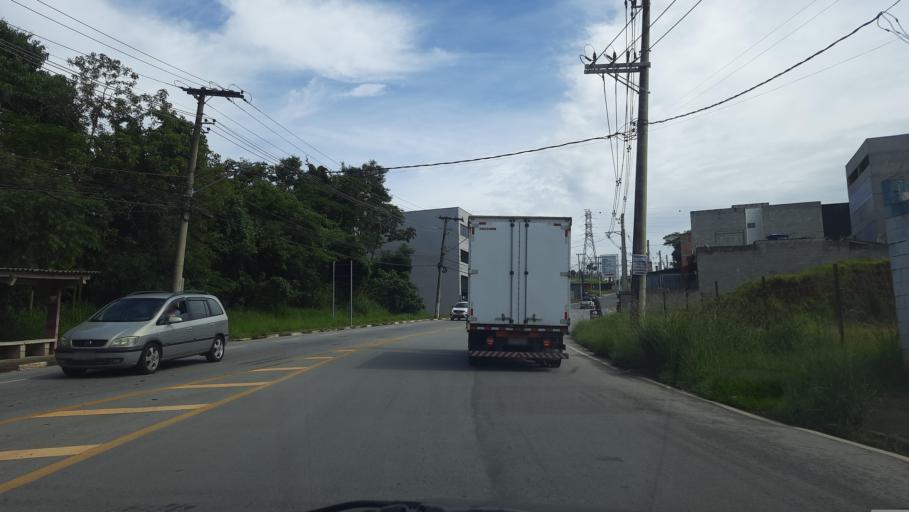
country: BR
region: Sao Paulo
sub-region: Caieiras
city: Caieiras
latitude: -23.3778
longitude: -46.7001
